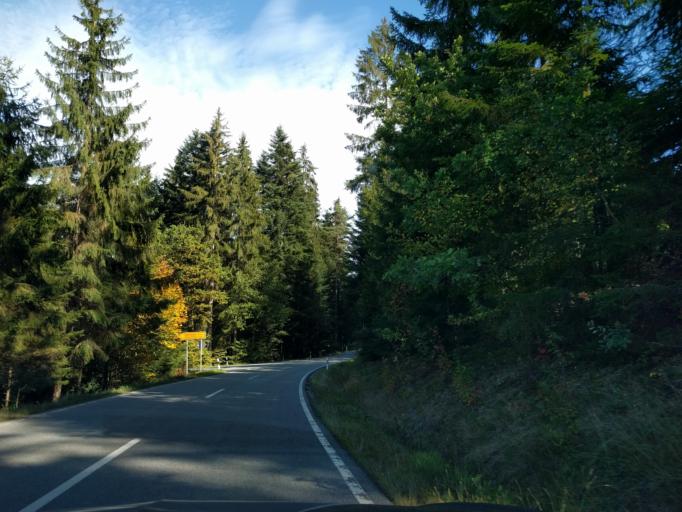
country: DE
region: Bavaria
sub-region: Lower Bavaria
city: Viechtach
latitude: 49.1254
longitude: 12.8880
